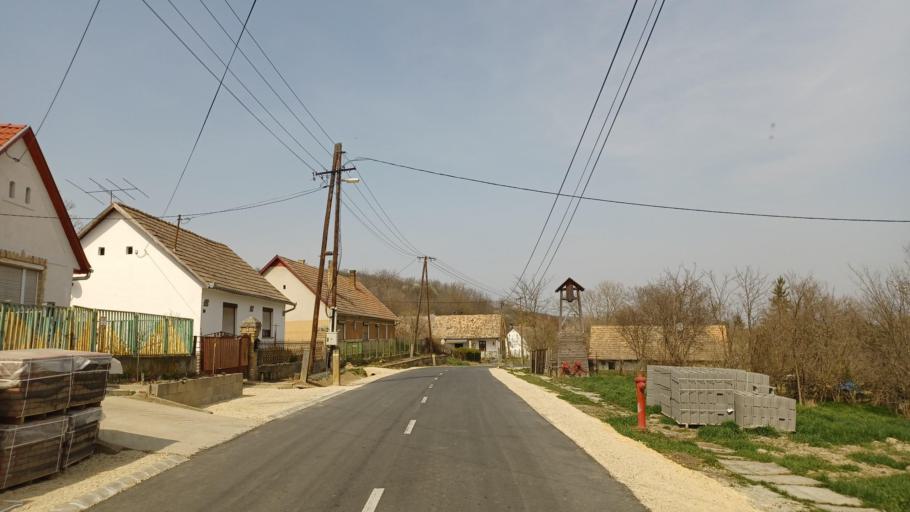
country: HU
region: Tolna
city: Nagydorog
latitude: 46.5551
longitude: 18.5901
